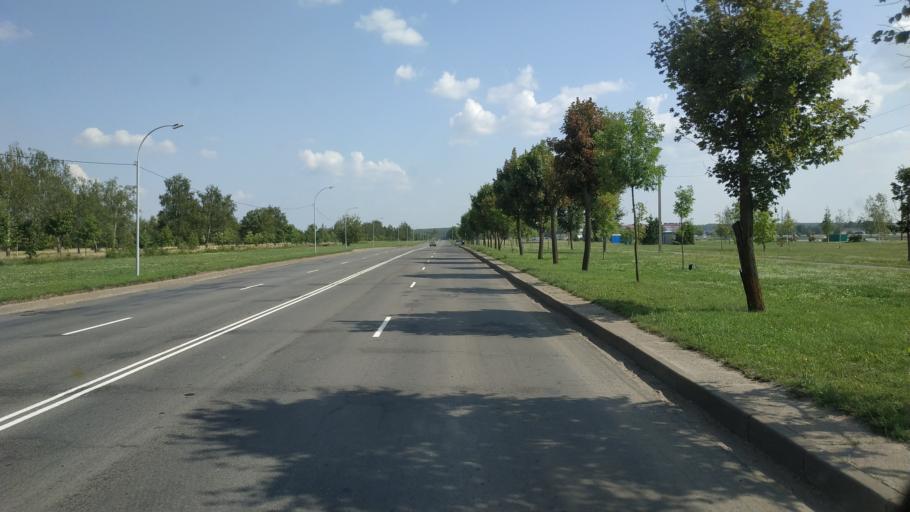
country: BY
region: Mogilev
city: Buynichy
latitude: 53.8632
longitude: 30.3202
